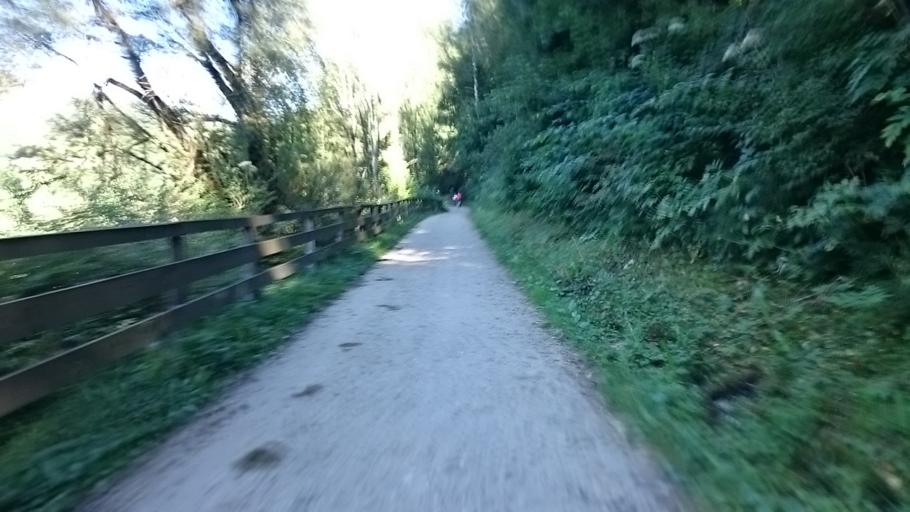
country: IT
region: Trentino-Alto Adige
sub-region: Bolzano
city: Rasun Anterselva - Rasen-Antholz
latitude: 46.7606
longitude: 12.0699
